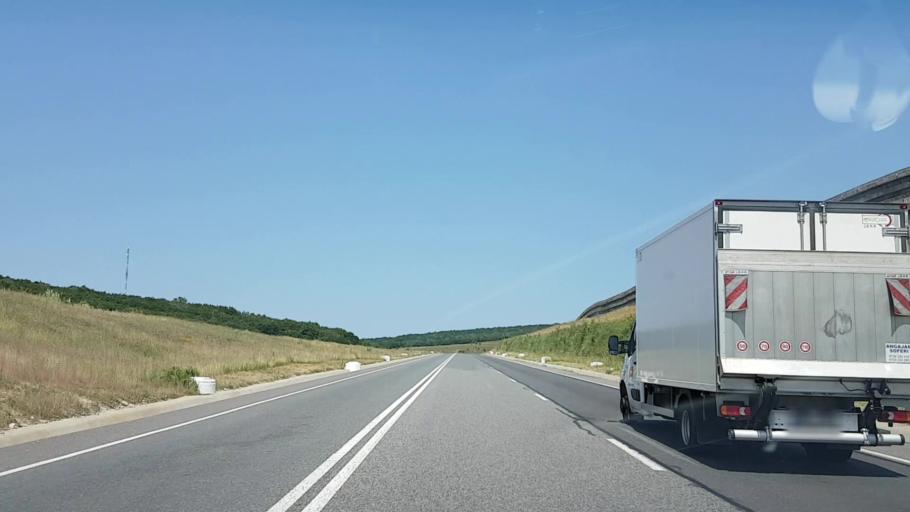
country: RO
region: Cluj
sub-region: Comuna Feleacu
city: Feleacu
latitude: 46.6977
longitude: 23.6375
